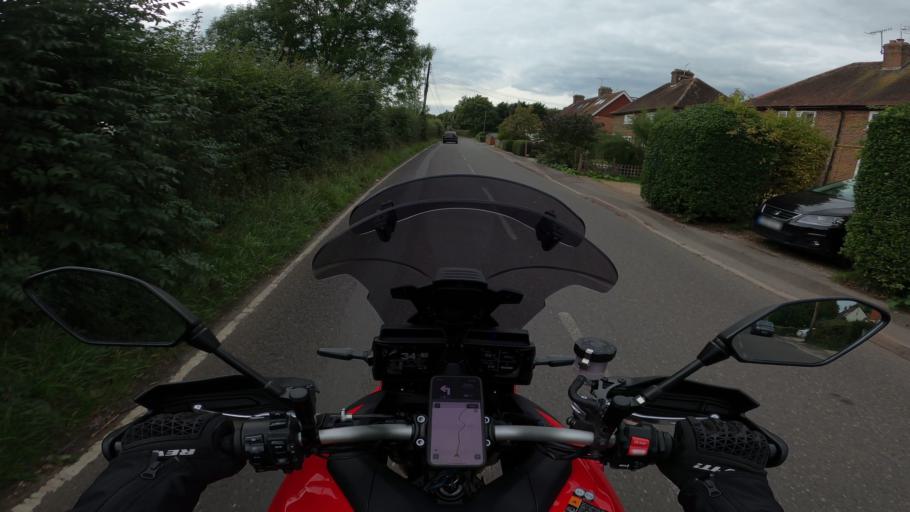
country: GB
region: England
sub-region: Kent
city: Edenbridge
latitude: 51.1947
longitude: 0.0578
